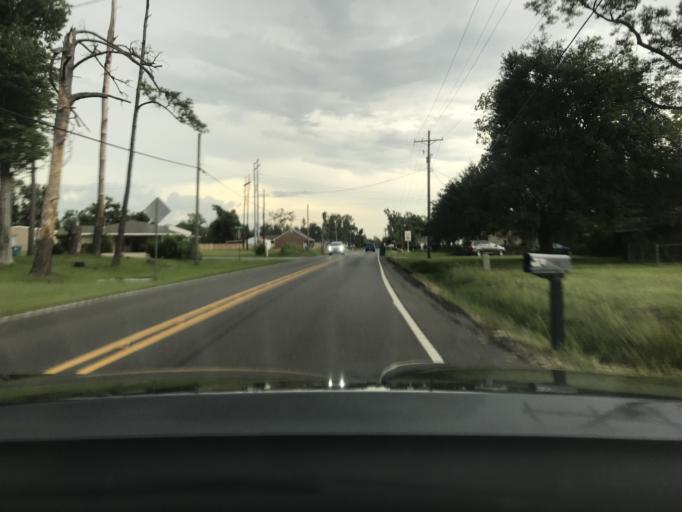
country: US
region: Louisiana
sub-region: Calcasieu Parish
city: Westlake
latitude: 30.2649
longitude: -93.2455
